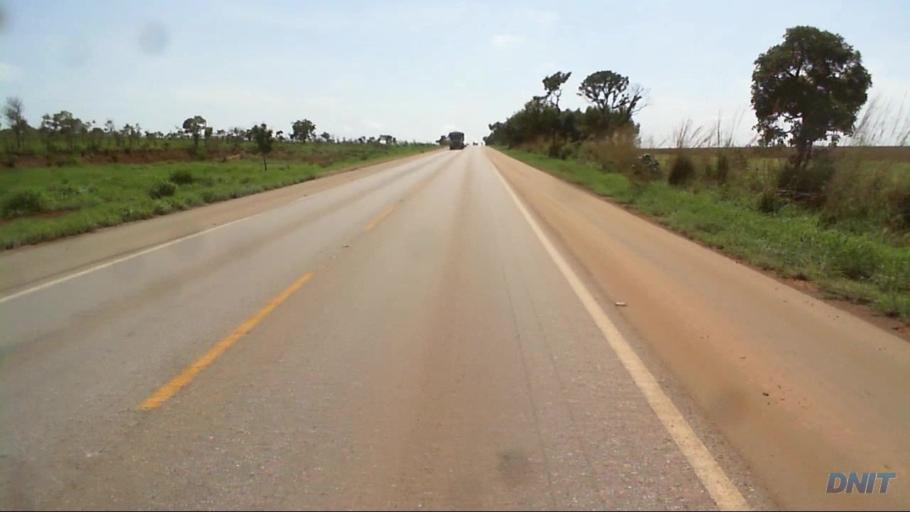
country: BR
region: Goias
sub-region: Barro Alto
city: Barro Alto
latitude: -15.2030
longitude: -48.7472
